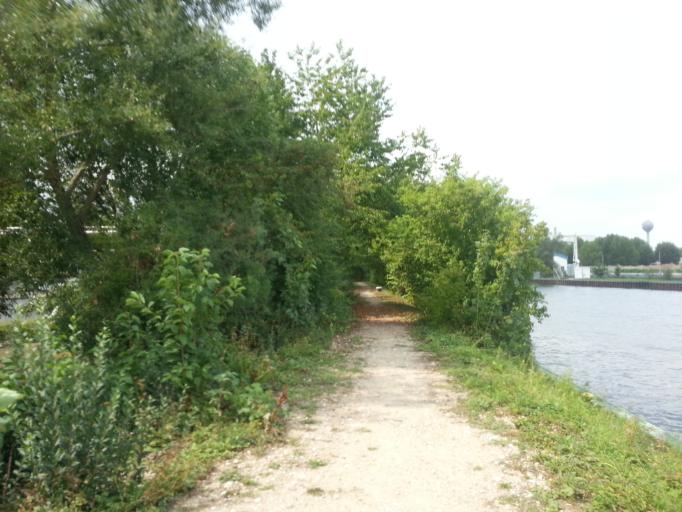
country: DE
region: Baden-Wuerttemberg
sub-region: Karlsruhe Region
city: Ilvesheim
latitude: 49.4794
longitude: 8.5820
